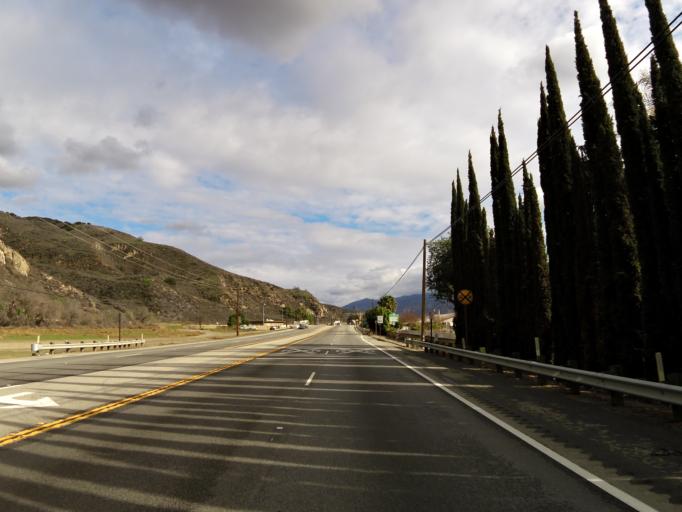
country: US
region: California
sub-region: Ventura County
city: Fillmore
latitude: 34.3985
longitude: -118.8976
